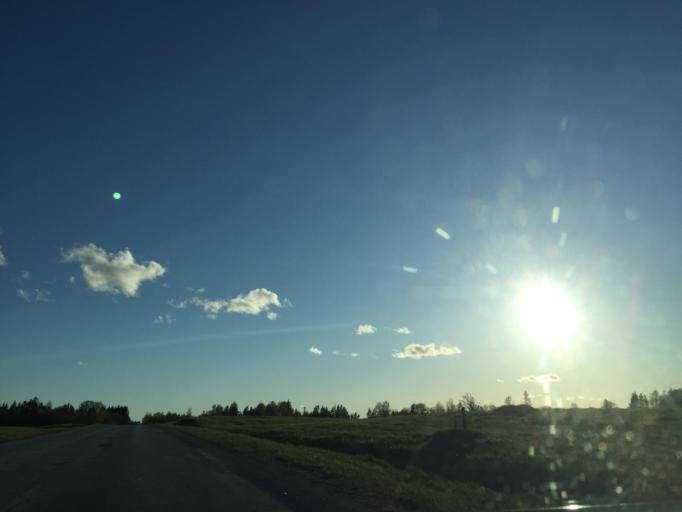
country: LV
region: Ergli
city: Ergli
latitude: 56.8726
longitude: 25.8115
